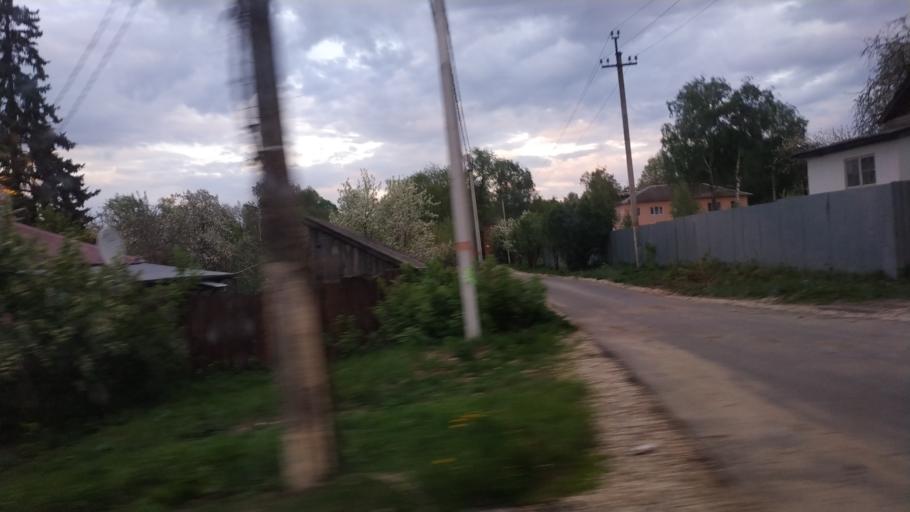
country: RU
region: Moskovskaya
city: Kashira
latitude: 54.8464
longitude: 38.1707
